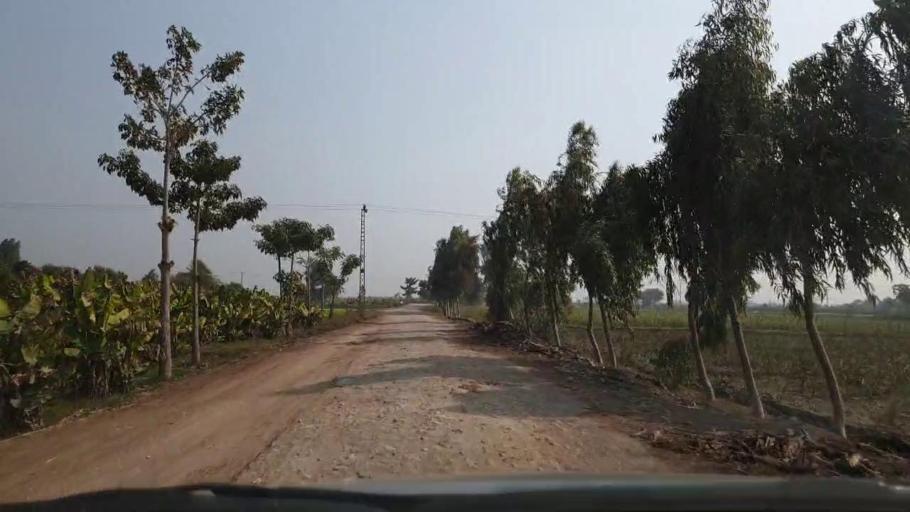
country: PK
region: Sindh
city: Matiari
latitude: 25.6534
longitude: 68.5507
